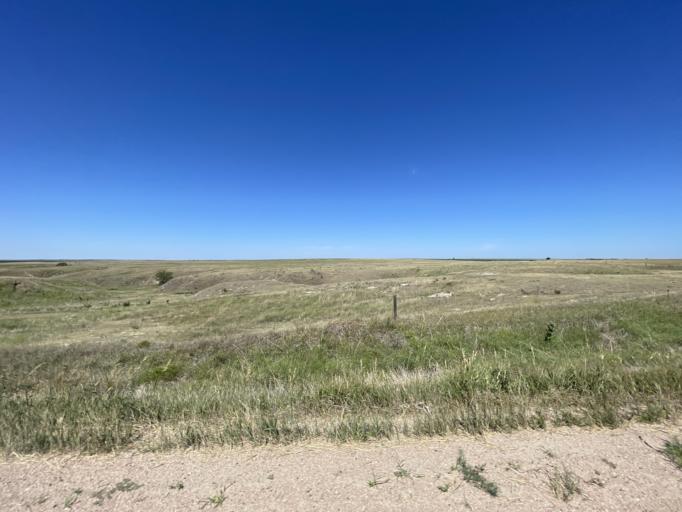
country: US
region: Nebraska
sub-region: Red Willow County
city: McCook
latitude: 40.4356
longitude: -100.7303
